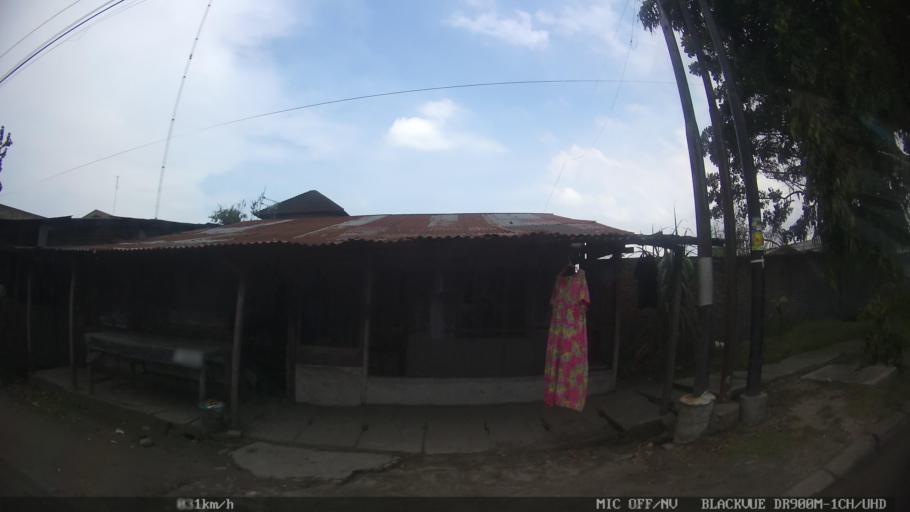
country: ID
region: North Sumatra
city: Medan
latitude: 3.6515
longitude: 98.6635
